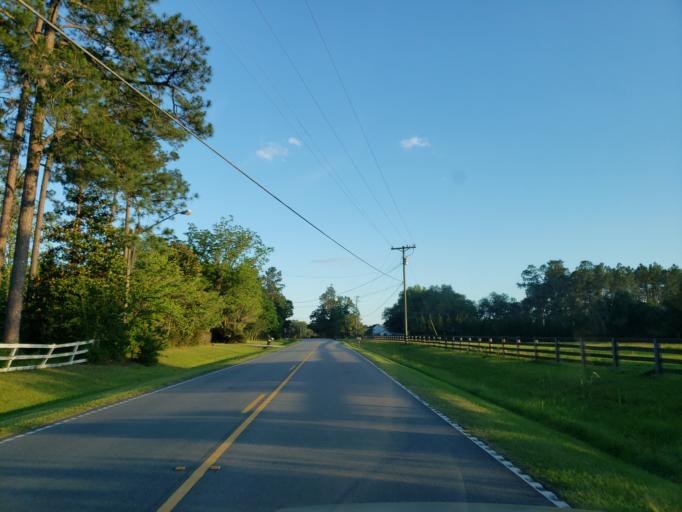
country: US
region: Georgia
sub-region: Lowndes County
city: Valdosta
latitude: 30.7403
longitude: -83.2516
